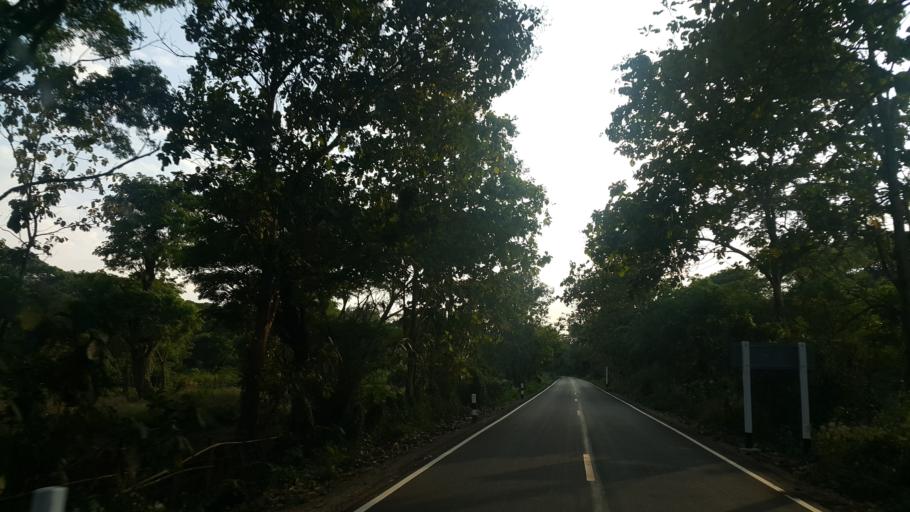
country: TH
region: Lampang
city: Sop Prap
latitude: 17.9345
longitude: 99.3401
